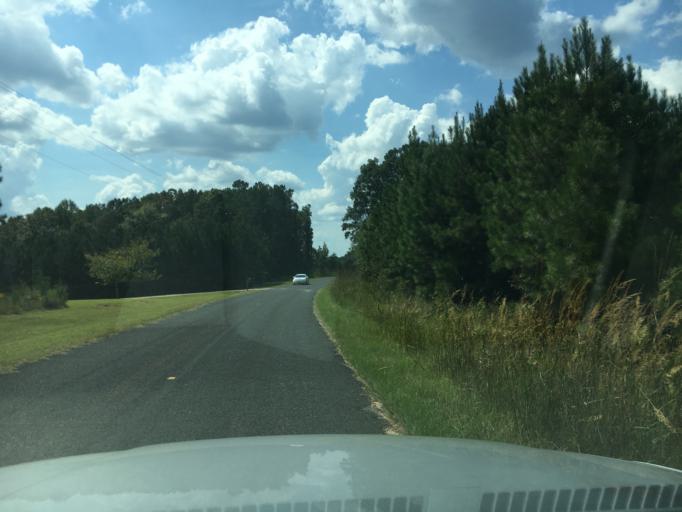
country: US
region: South Carolina
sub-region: Greenwood County
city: Greenwood
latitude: 34.0631
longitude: -82.1474
